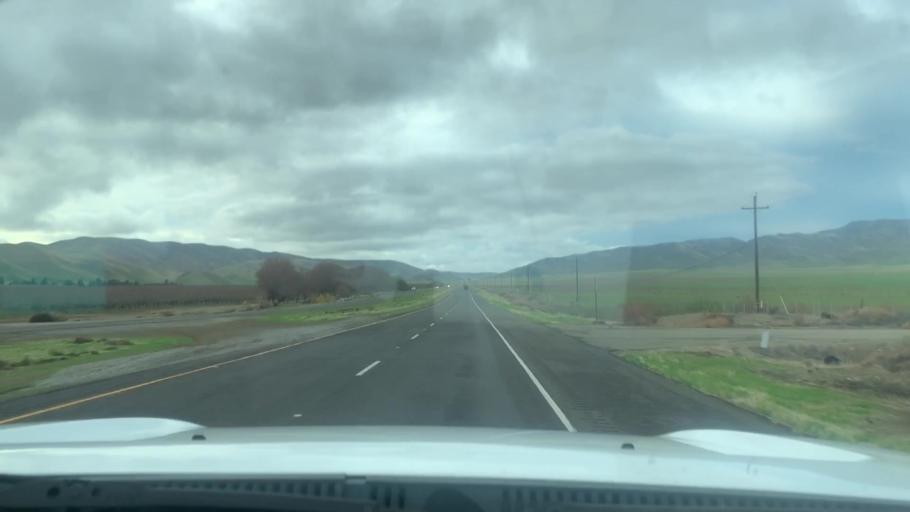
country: US
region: California
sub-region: San Luis Obispo County
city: Shandon
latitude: 35.6769
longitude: -120.0938
